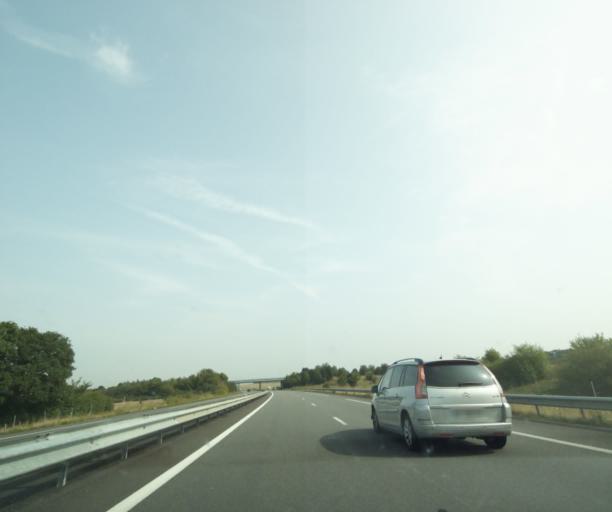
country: FR
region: Pays de la Loire
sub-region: Departement de la Sarthe
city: Saint-Paterne
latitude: 48.4222
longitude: 0.1364
